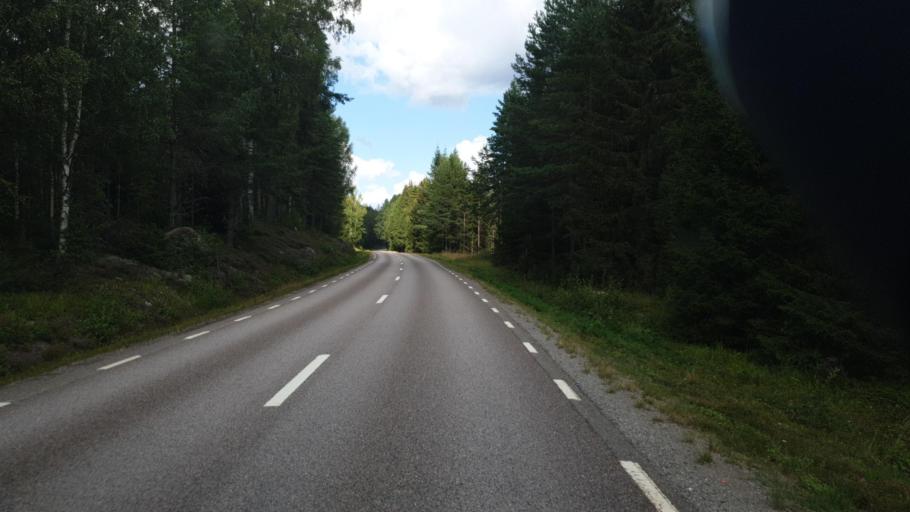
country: SE
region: Vaermland
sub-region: Eda Kommun
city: Amotfors
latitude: 59.6286
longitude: 12.3416
